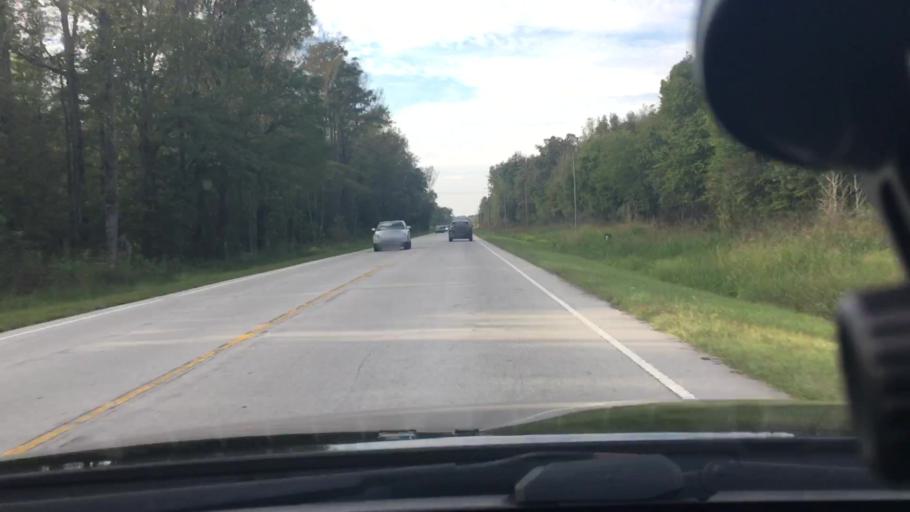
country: US
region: North Carolina
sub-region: Pitt County
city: Windsor
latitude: 35.4881
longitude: -77.3045
